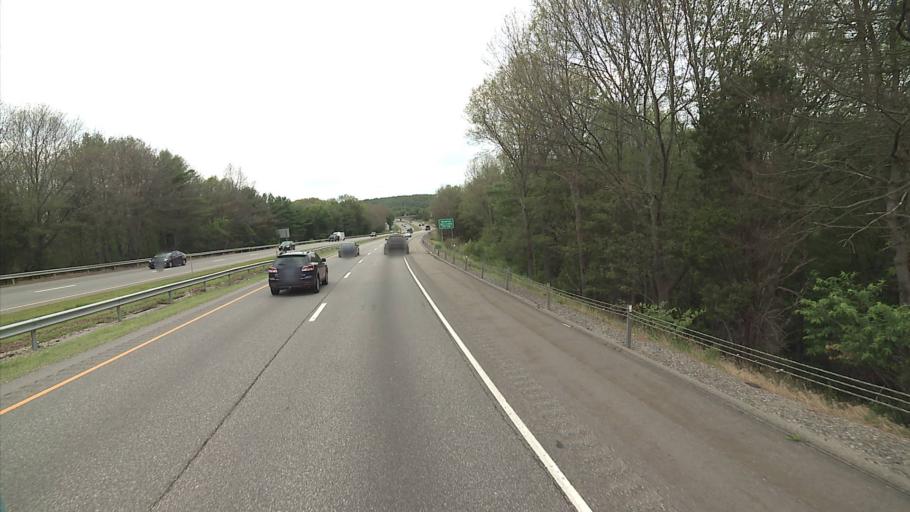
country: US
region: Connecticut
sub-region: New London County
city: Montville Center
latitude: 41.4998
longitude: -72.1157
